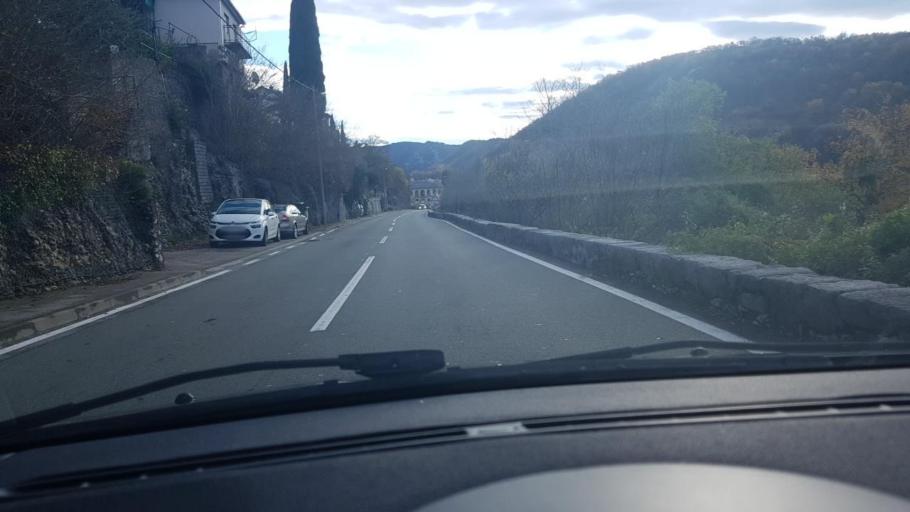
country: HR
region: Primorsko-Goranska
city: Cavle
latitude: 45.3390
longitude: 14.4656
